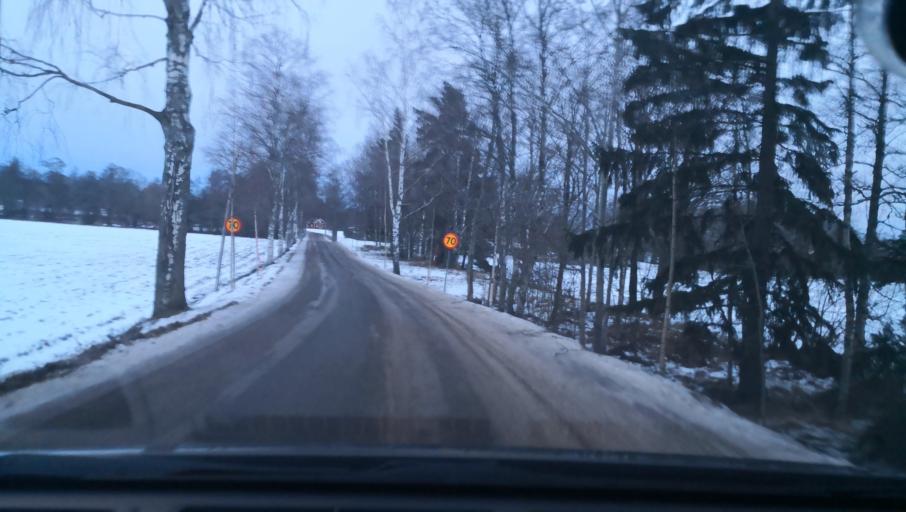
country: SE
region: Dalarna
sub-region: Avesta Kommun
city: Horndal
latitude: 60.2004
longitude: 16.4806
